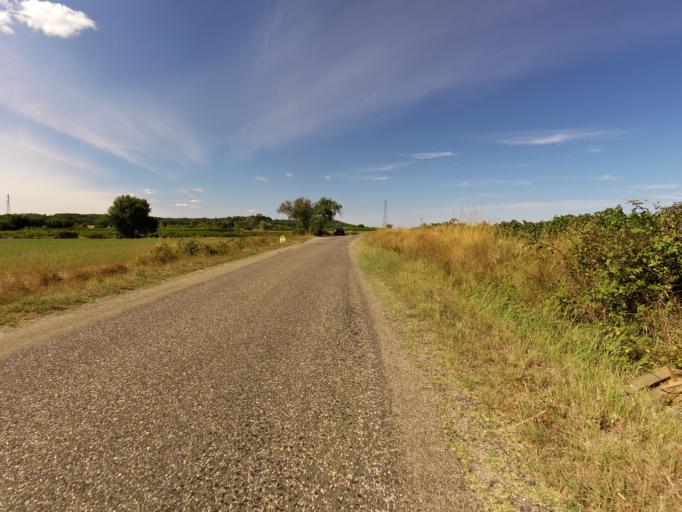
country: FR
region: Languedoc-Roussillon
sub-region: Departement du Gard
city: Lezan
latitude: 43.9660
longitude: 4.0255
